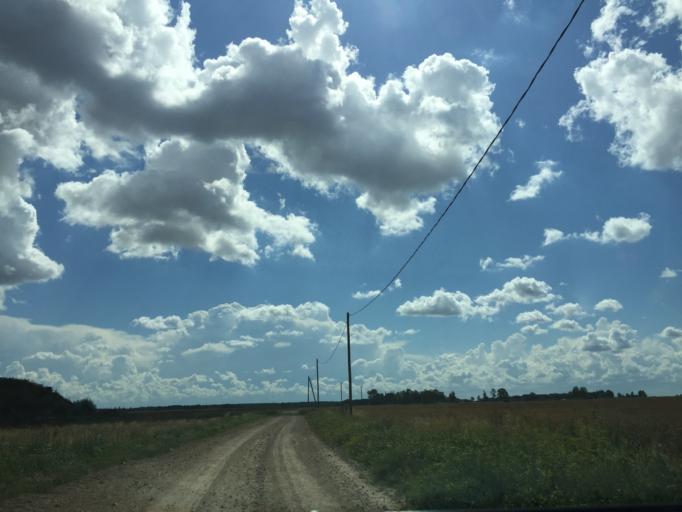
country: LV
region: Rundales
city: Pilsrundale
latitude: 56.3417
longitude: 23.9736
